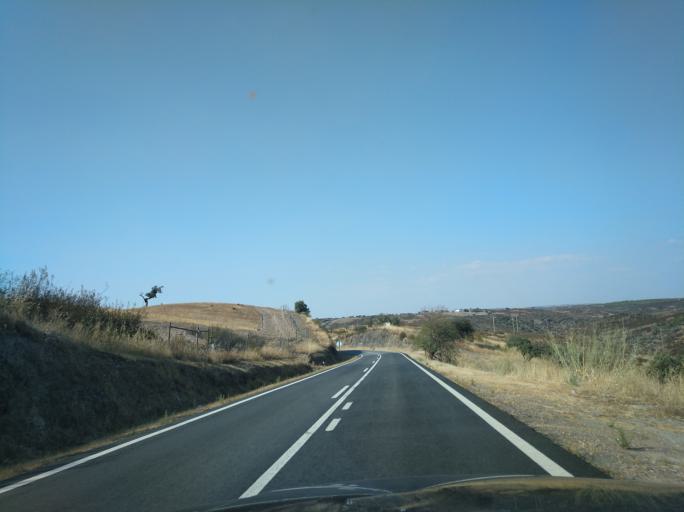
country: ES
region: Extremadura
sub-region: Provincia de Badajoz
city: Valencia del Mombuey
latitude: 38.1460
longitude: -7.2370
